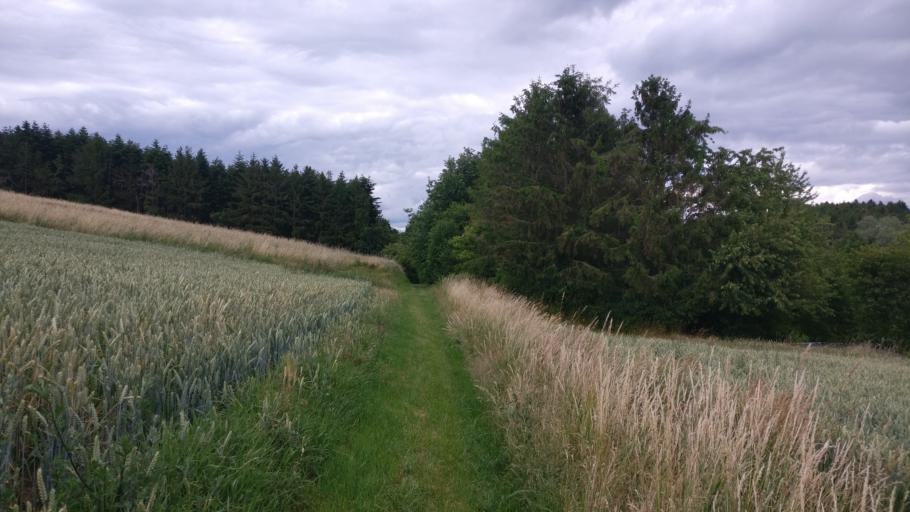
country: DK
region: Capital Region
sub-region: Egedal Kommune
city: Vekso
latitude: 55.7566
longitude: 12.2265
